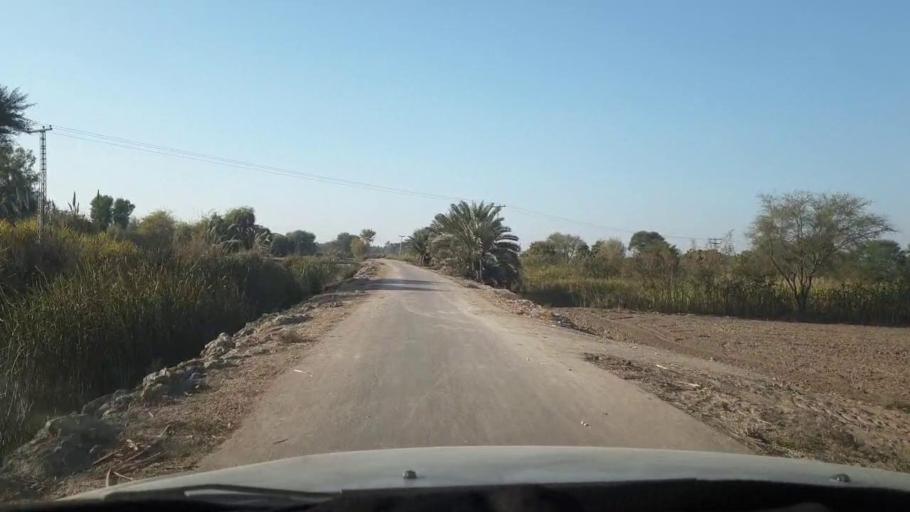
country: PK
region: Sindh
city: Adilpur
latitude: 27.9368
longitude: 69.2596
